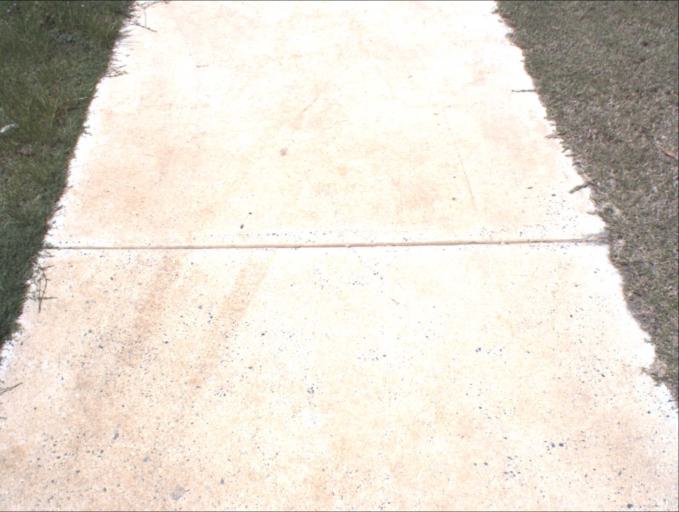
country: AU
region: Queensland
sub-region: Logan
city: Chambers Flat
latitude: -27.8056
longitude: 153.1120
